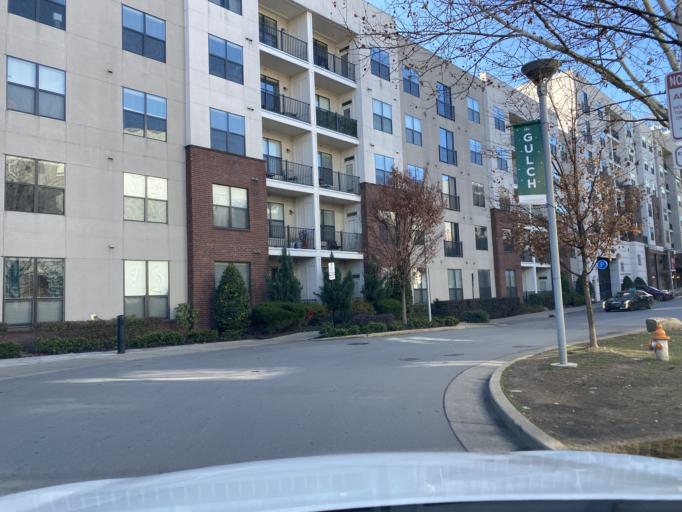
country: US
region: Tennessee
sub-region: Davidson County
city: Nashville
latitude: 36.1528
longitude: -86.7823
